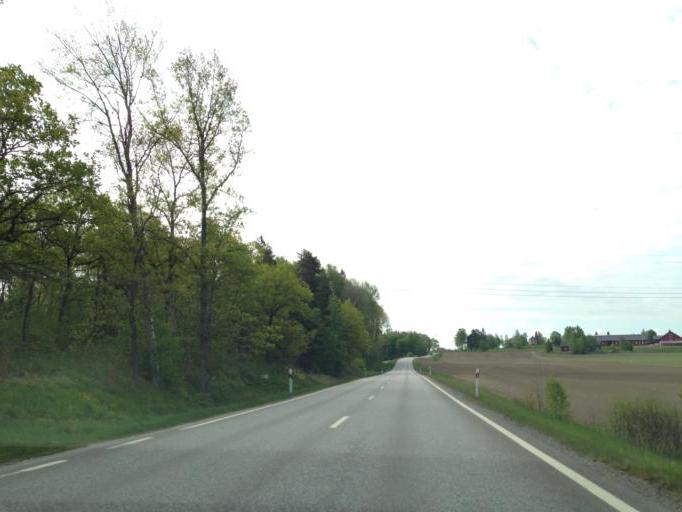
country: SE
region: Soedermanland
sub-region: Flens Kommun
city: Malmkoping
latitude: 59.0936
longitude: 16.8051
